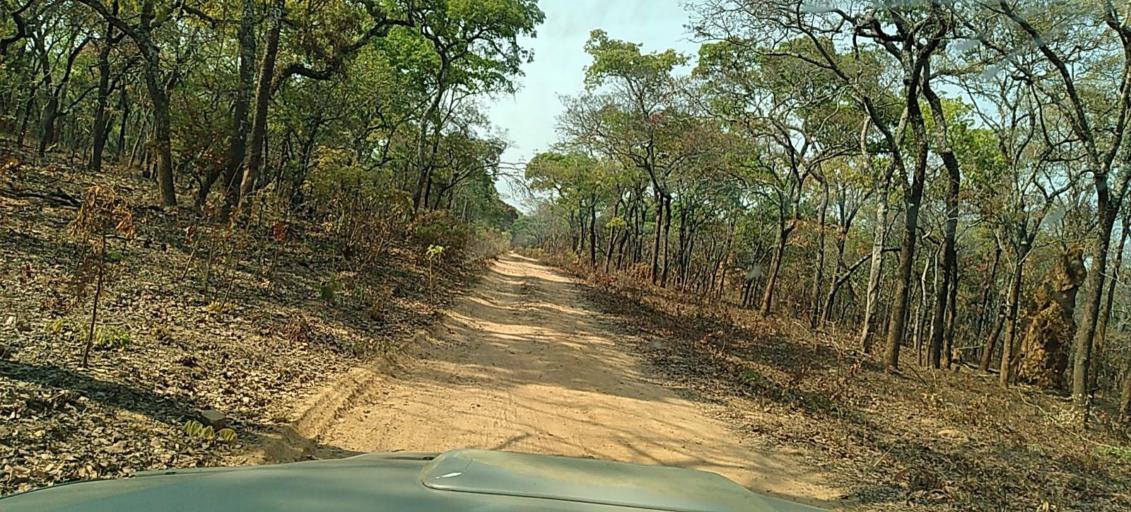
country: ZM
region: North-Western
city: Kasempa
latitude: -13.5276
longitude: 26.4097
